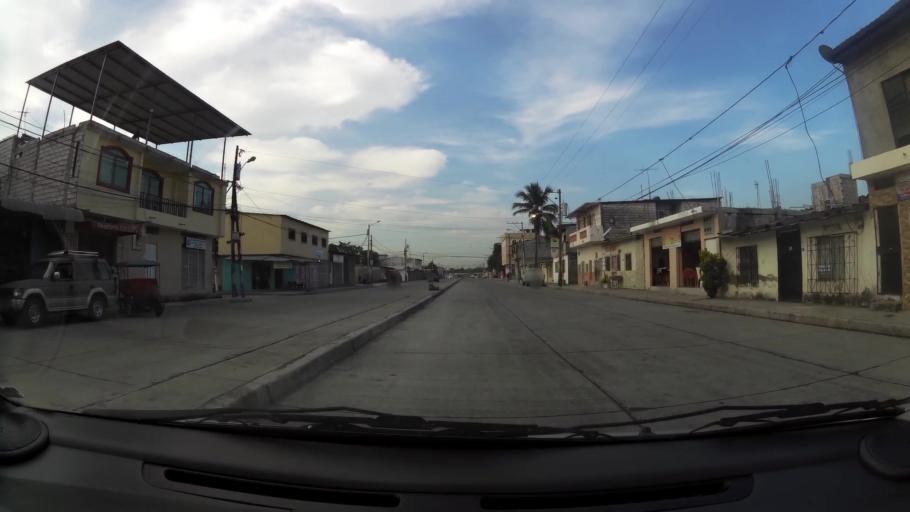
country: EC
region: Guayas
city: Eloy Alfaro
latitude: -2.0927
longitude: -79.9033
